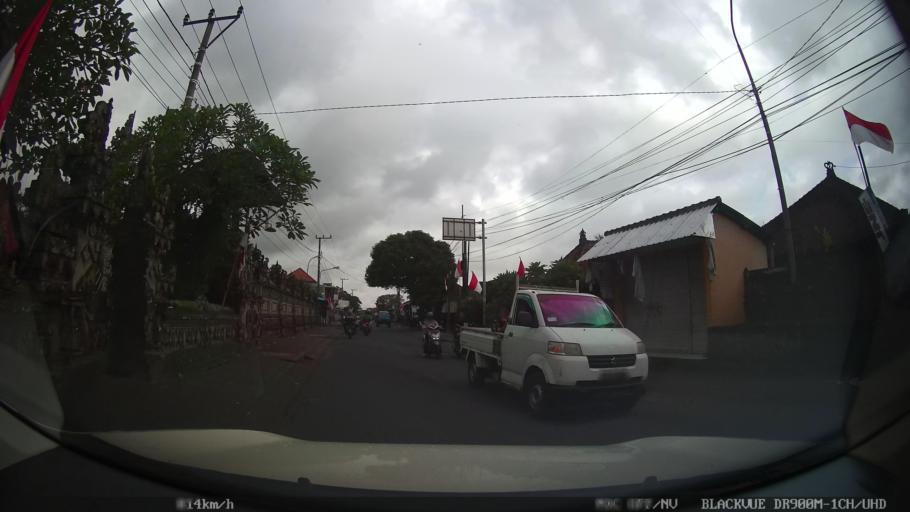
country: ID
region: Bali
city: Banjar Mambalkajanan
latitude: -8.5494
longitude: 115.2204
